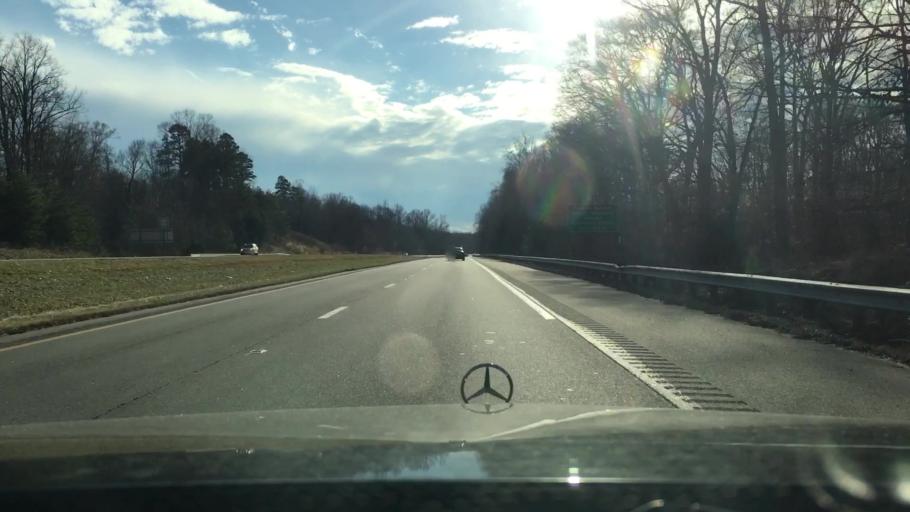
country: US
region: Virginia
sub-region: City of Danville
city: Danville
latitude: 36.5535
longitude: -79.3912
